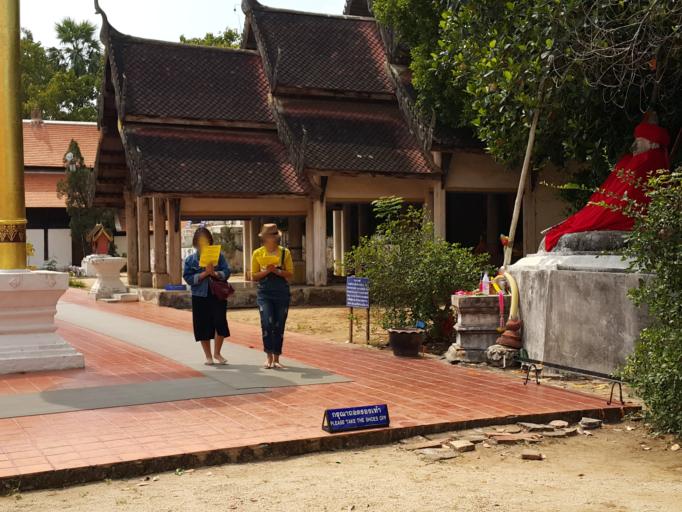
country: TH
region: Lampang
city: Ko Kha
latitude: 18.2176
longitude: 99.3888
